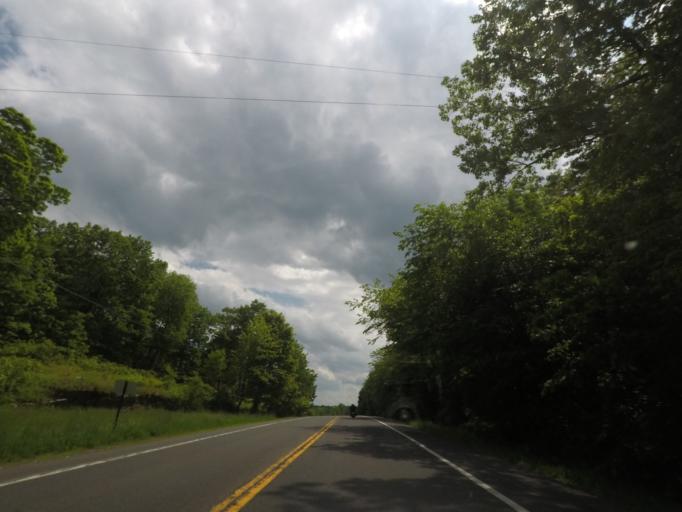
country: US
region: New York
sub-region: Dutchess County
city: Pine Plains
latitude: 42.0945
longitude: -73.6893
